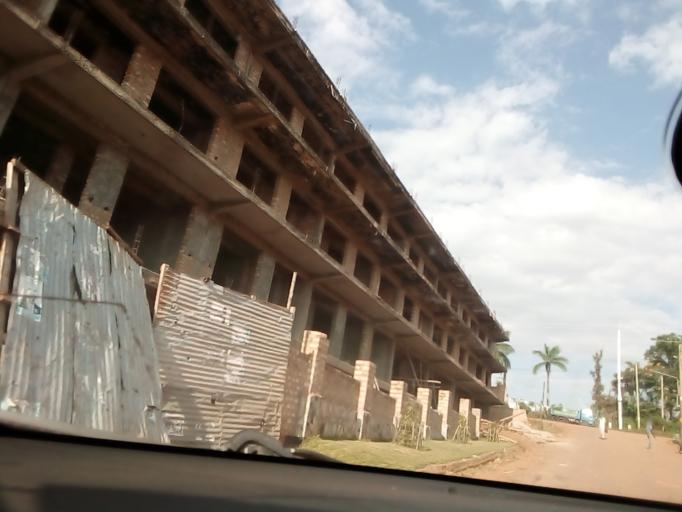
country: UG
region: Central Region
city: Masaka
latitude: -0.3507
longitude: 31.7408
